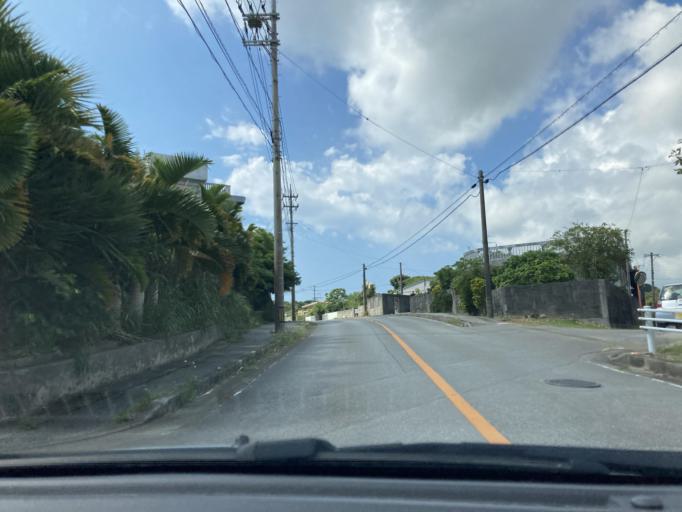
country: JP
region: Okinawa
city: Tomigusuku
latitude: 26.1495
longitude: 127.7913
